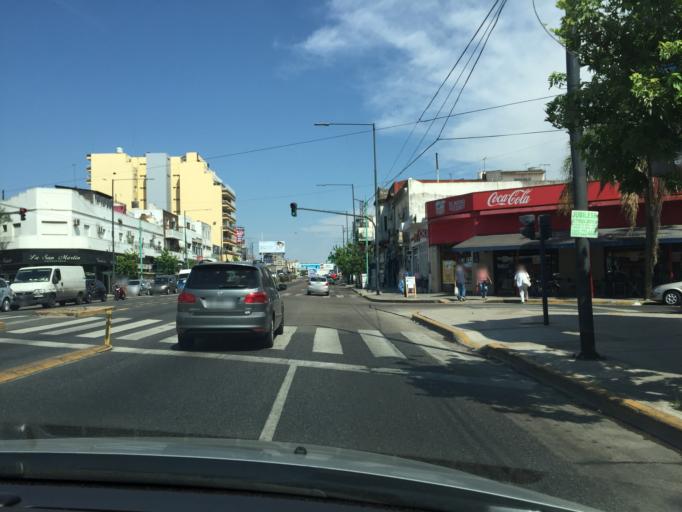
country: AR
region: Buenos Aires
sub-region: Partido de General San Martin
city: General San Martin
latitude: -34.5900
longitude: -58.5162
